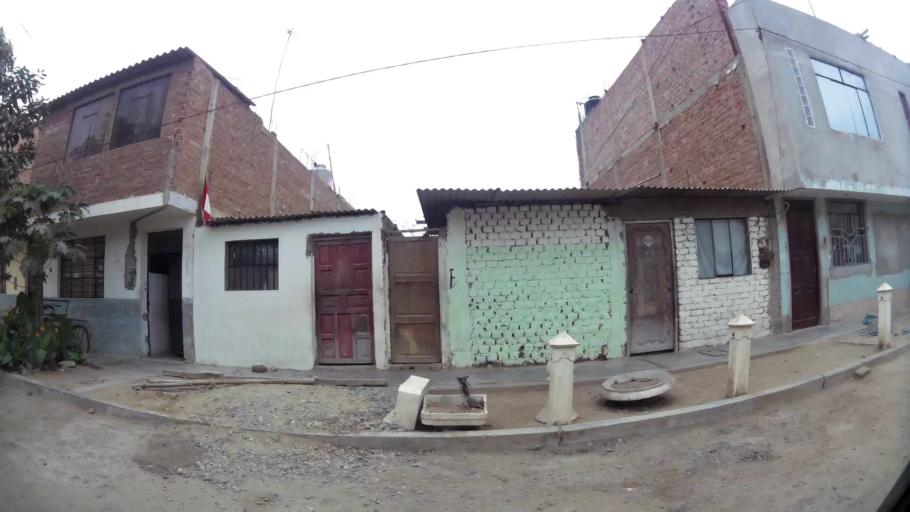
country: PE
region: La Libertad
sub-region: Provincia de Trujillo
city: La Esperanza
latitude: -8.0965
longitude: -79.0634
